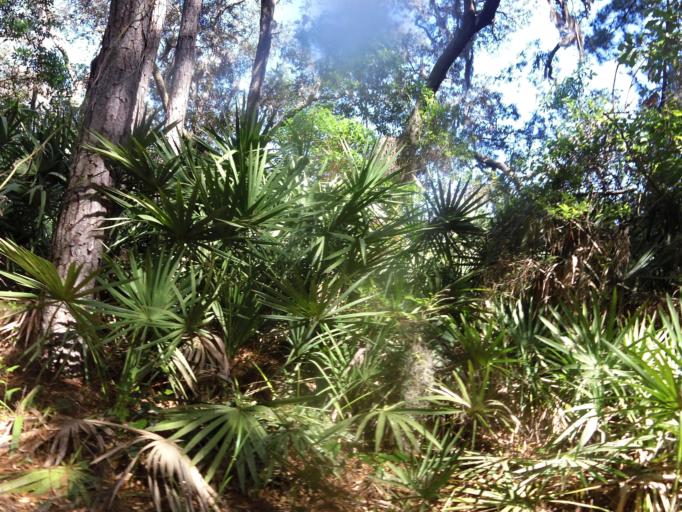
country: US
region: Florida
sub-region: Duval County
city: Atlantic Beach
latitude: 30.4533
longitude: -81.4814
